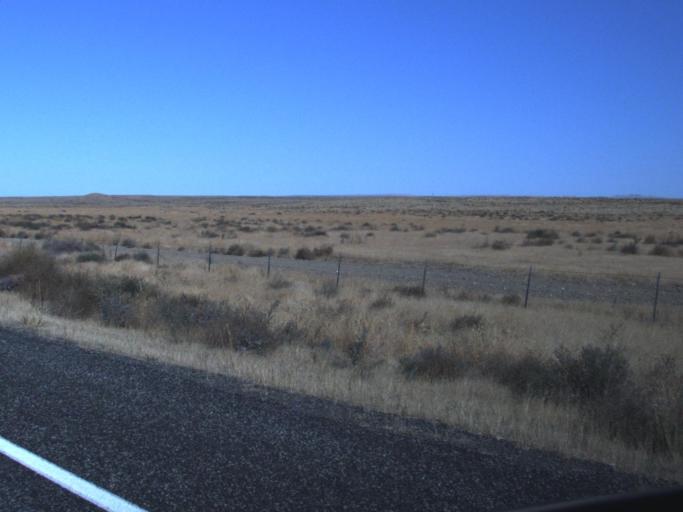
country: US
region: Washington
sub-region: Benton County
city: Benton City
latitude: 46.4696
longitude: -119.5469
